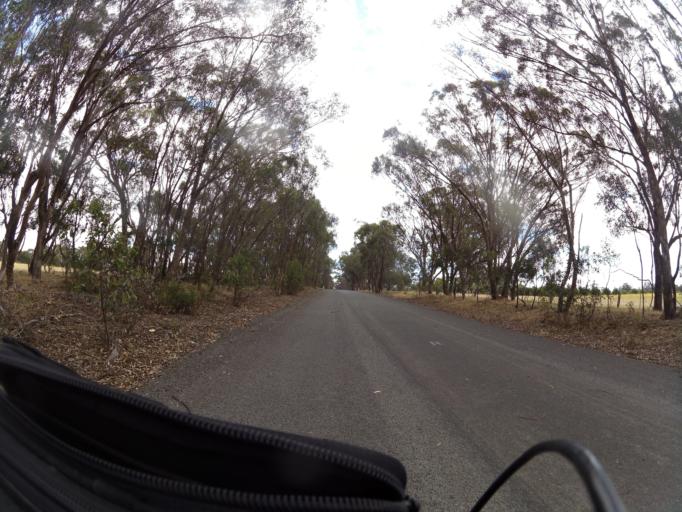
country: AU
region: Victoria
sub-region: Greater Shepparton
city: Shepparton
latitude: -36.7311
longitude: 145.1539
